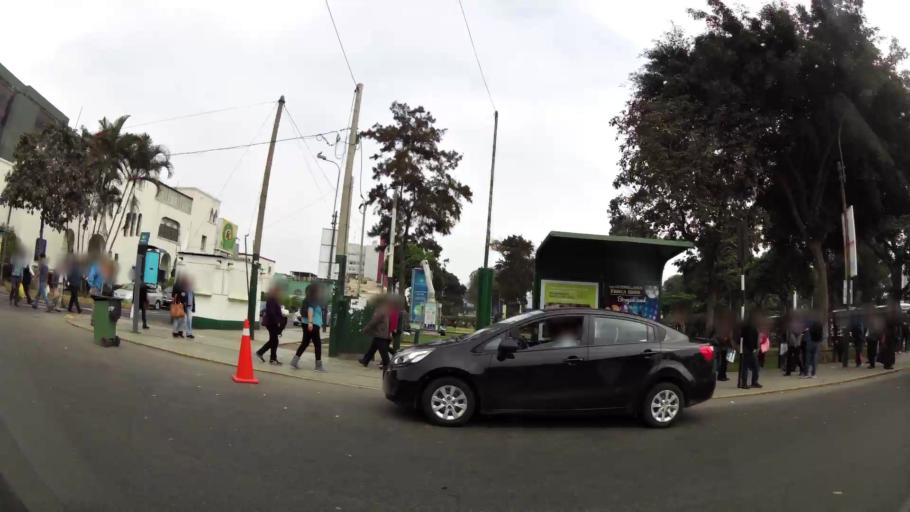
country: PE
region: Lima
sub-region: Lima
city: San Isidro
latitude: -12.0798
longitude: -77.0418
